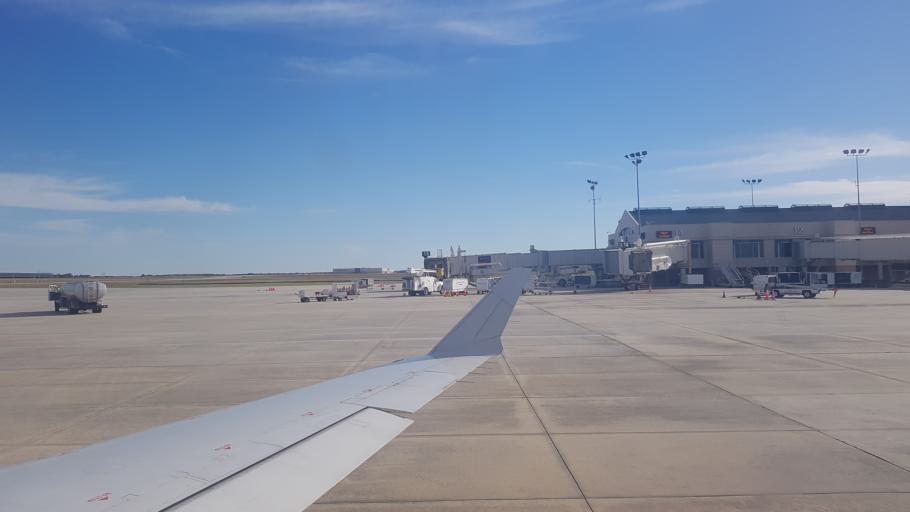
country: US
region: Georgia
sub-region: Chatham County
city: Port Wentworth
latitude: 32.1367
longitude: -81.2060
